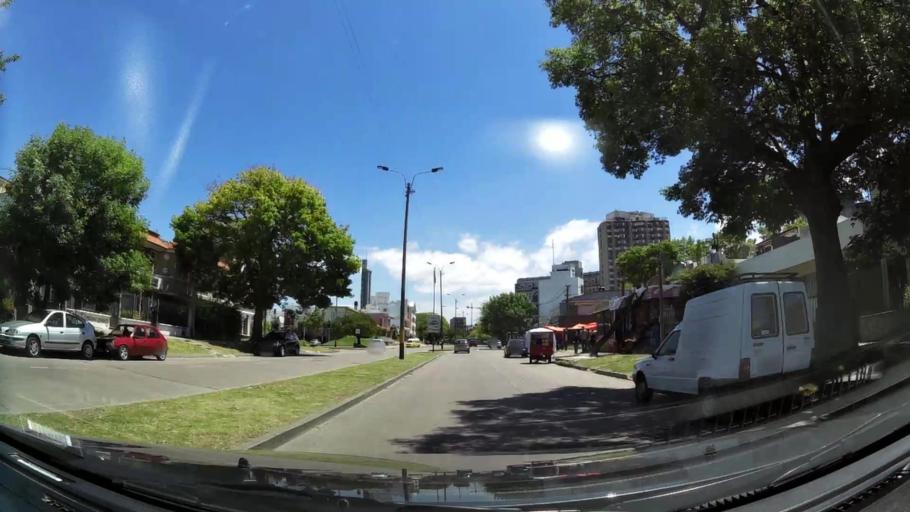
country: UY
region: Montevideo
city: Montevideo
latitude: -34.8953
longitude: -56.1483
